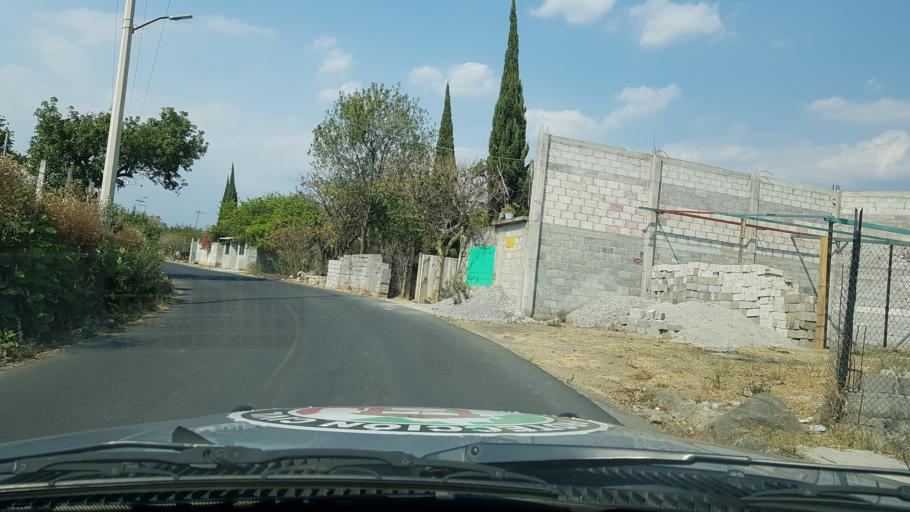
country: MX
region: Mexico
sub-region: Atlautla
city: San Andres Tlalamac
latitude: 18.9718
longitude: -98.8159
